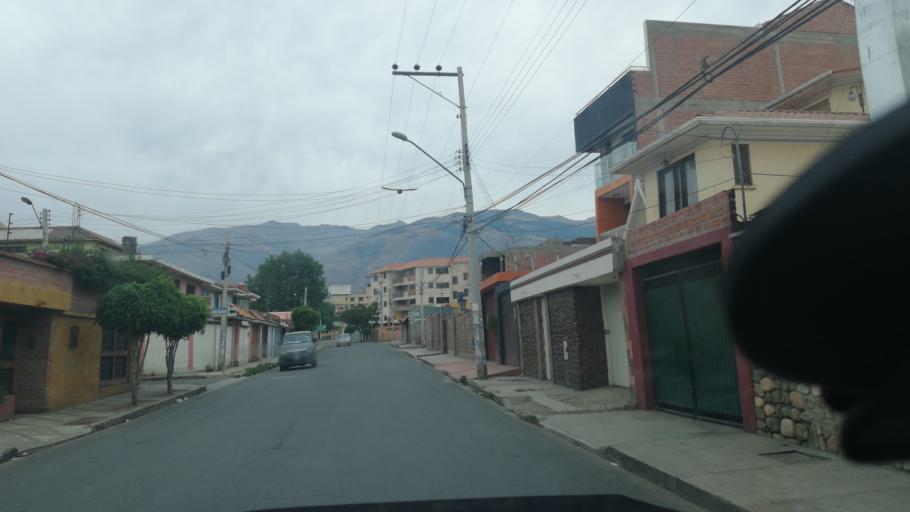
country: BO
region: Cochabamba
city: Cochabamba
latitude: -17.3692
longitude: -66.1884
